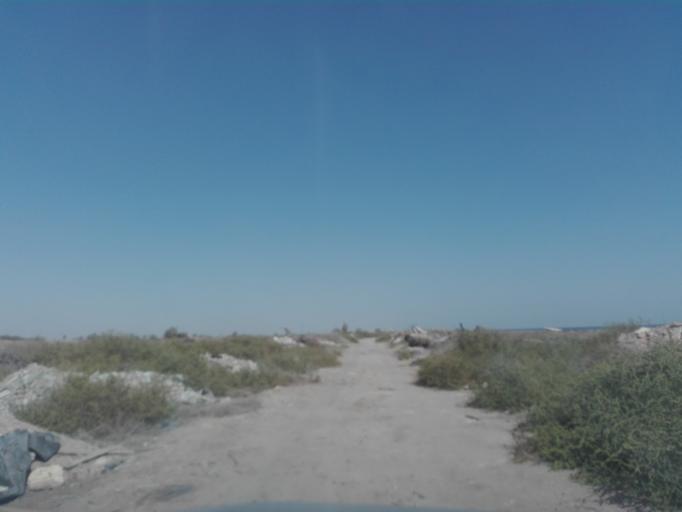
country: TN
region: Qabis
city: Gabes
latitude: 33.9663
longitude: 10.0639
